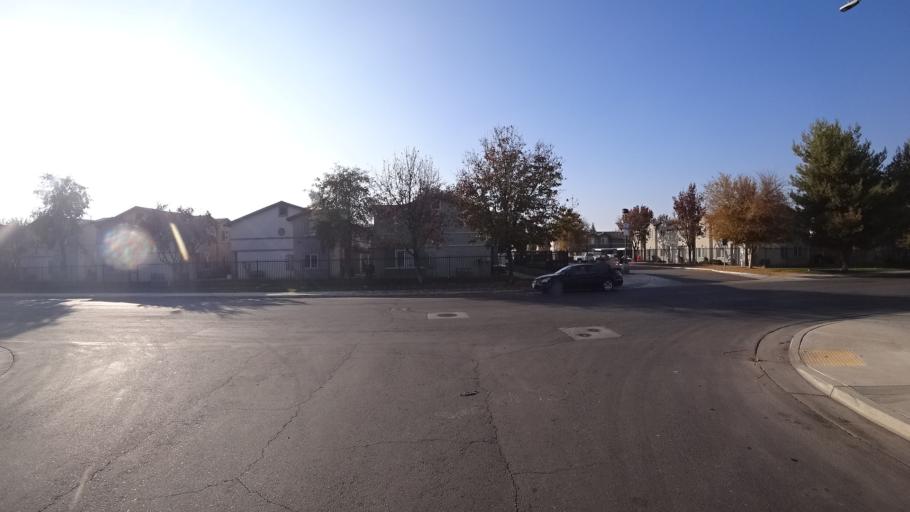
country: US
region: California
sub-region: Kern County
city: Greenfield
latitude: 35.2839
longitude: -119.0073
